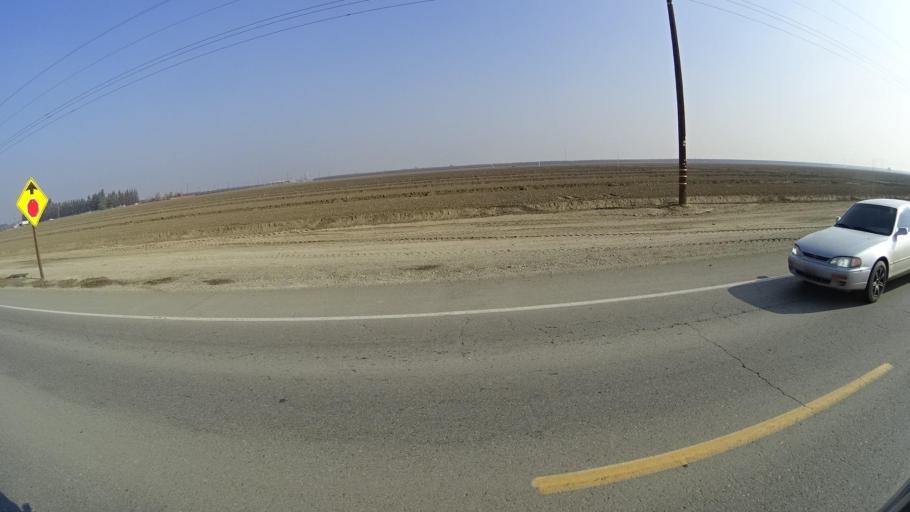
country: US
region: California
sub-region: Kern County
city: Greenfield
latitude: 35.2058
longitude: -119.1102
